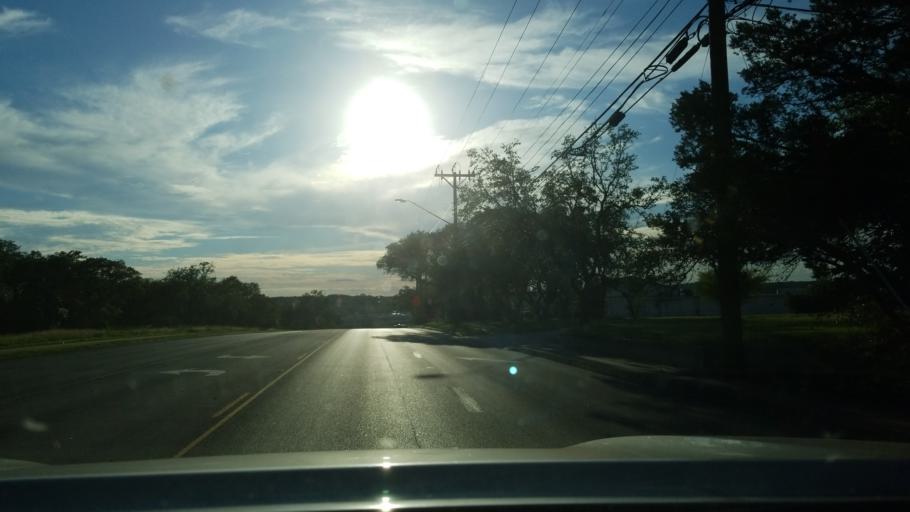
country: US
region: Texas
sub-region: Bexar County
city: Hollywood Park
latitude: 29.6205
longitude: -98.4615
